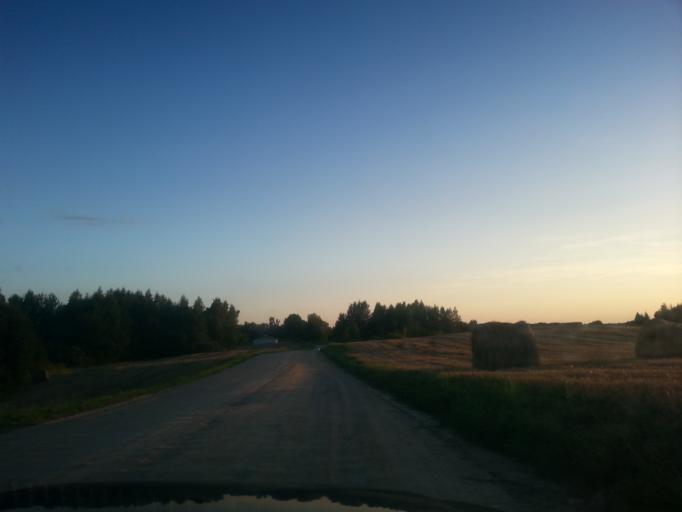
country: BY
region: Minsk
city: Narach
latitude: 54.9792
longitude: 26.6480
